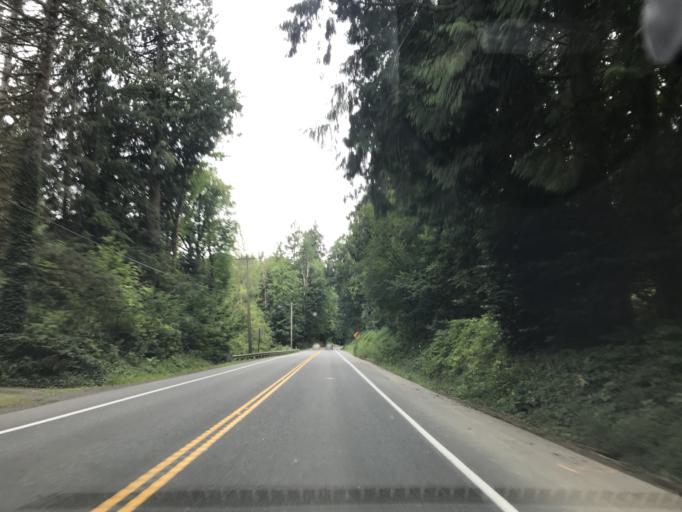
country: US
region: Washington
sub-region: King County
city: Fall City
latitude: 47.5357
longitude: -121.9147
